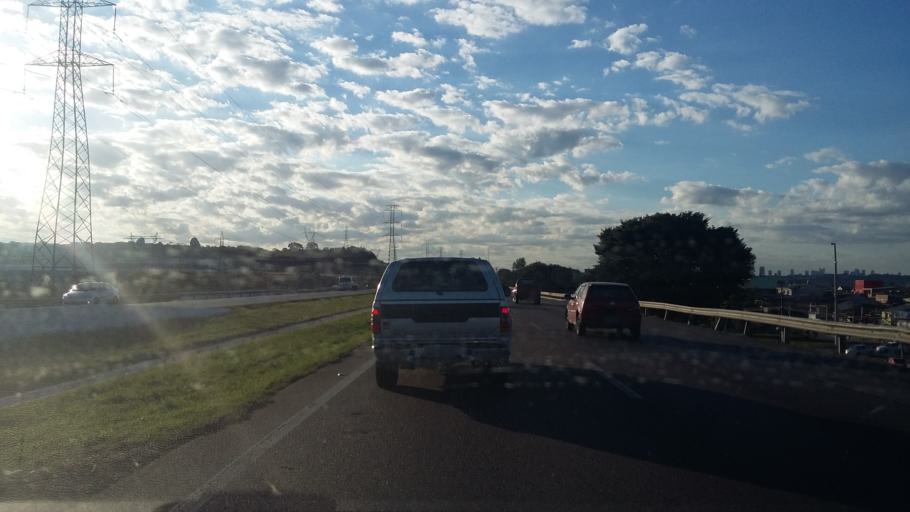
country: BR
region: Parana
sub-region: Araucaria
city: Araucaria
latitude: -25.5157
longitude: -49.3366
